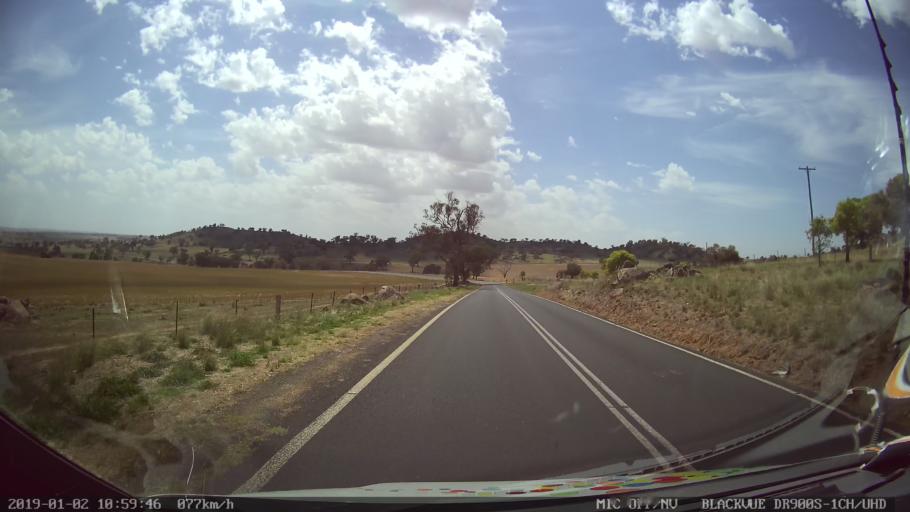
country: AU
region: New South Wales
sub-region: Cootamundra
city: Cootamundra
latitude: -34.6123
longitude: 148.3098
